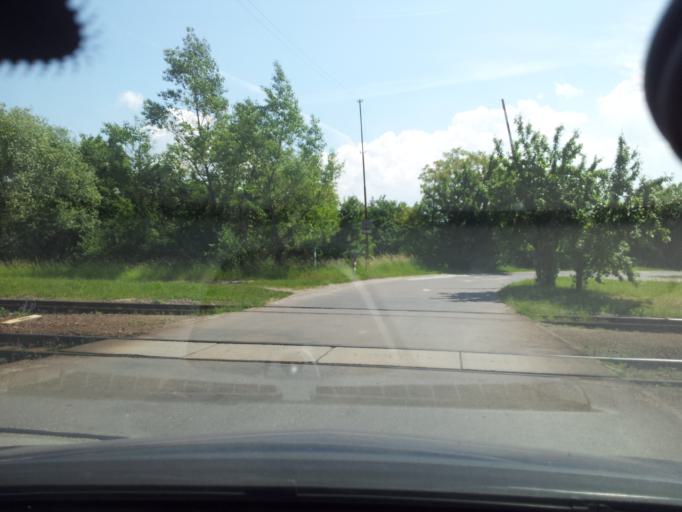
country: SK
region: Nitriansky
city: Novaky
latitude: 48.6862
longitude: 18.5200
